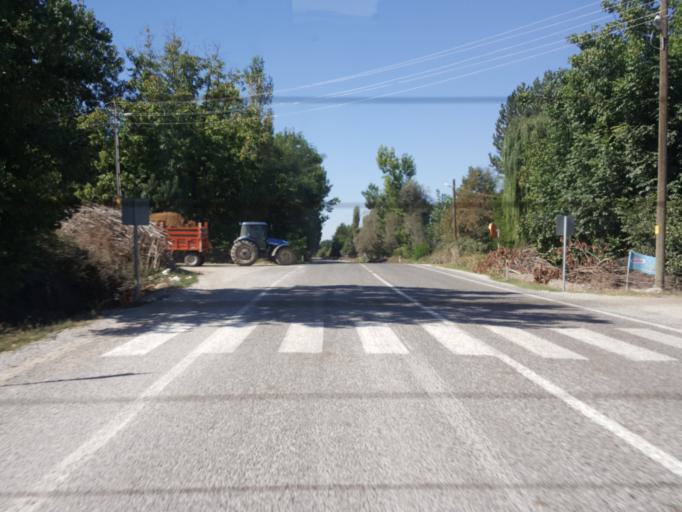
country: TR
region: Tokat
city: Pazar
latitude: 40.2701
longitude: 36.2409
